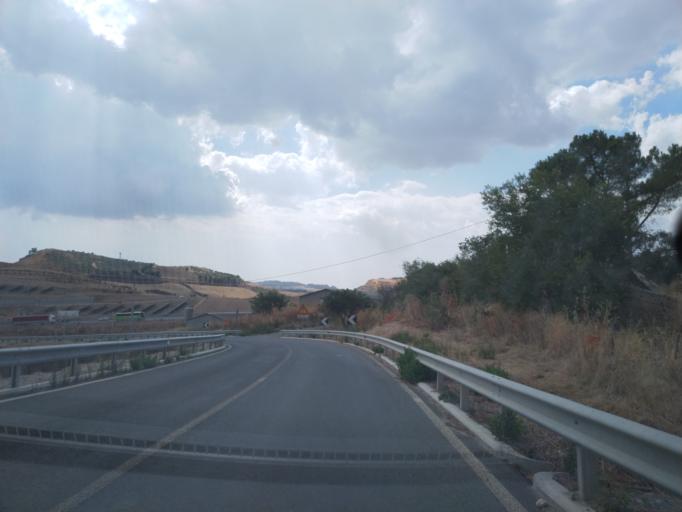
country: IT
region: Sicily
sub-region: Provincia di Caltanissetta
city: San Cataldo
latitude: 37.4504
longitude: 13.9730
